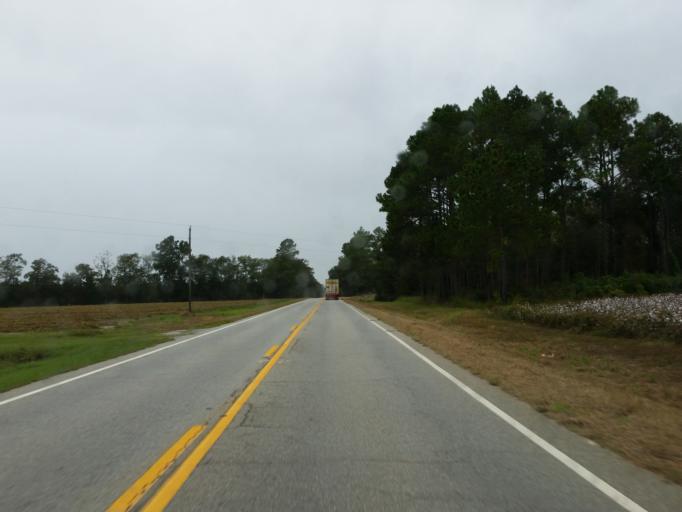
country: US
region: Georgia
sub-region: Berrien County
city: Ray City
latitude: 31.0931
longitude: -83.2551
